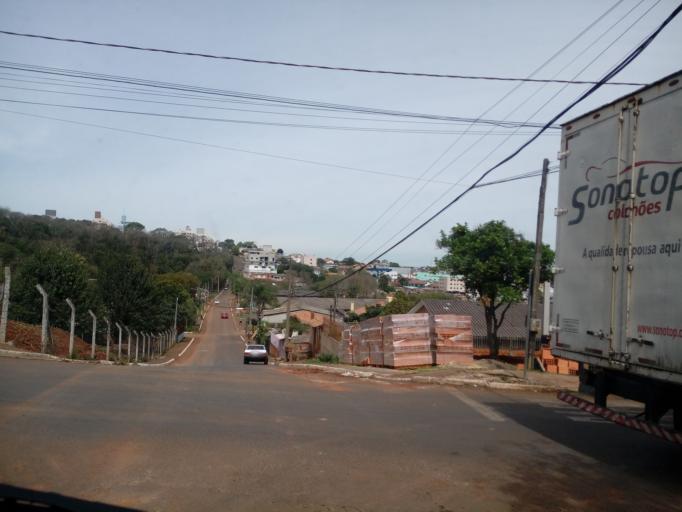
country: BR
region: Santa Catarina
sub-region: Chapeco
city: Chapeco
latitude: -27.0711
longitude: -52.6173
